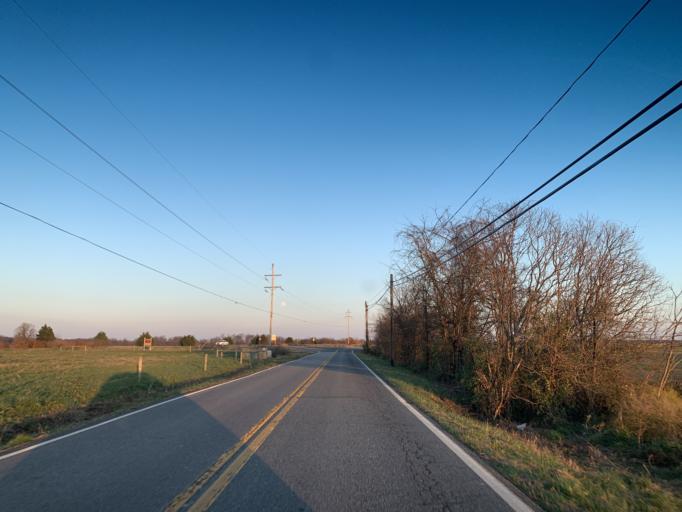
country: US
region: Maryland
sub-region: Cecil County
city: Charlestown
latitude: 39.4109
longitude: -75.9125
